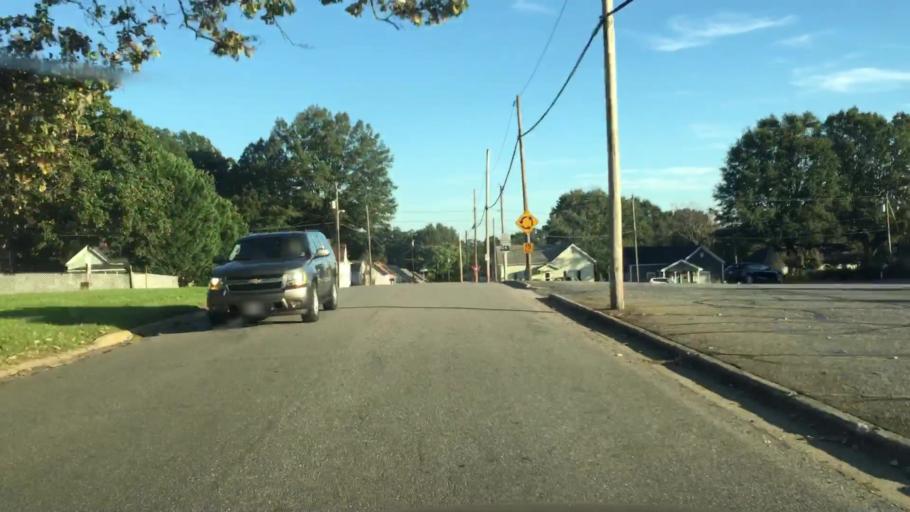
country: US
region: North Carolina
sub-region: Iredell County
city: Mooresville
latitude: 35.5773
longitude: -80.8182
